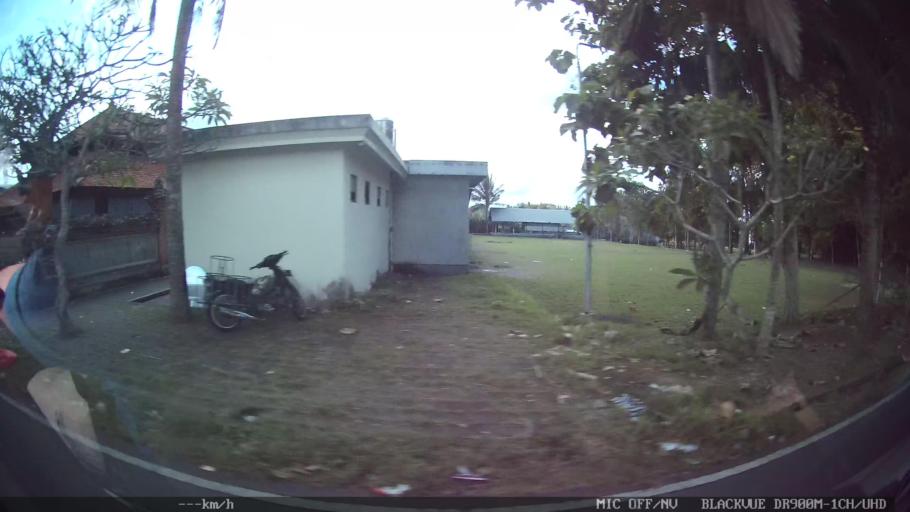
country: ID
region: Bali
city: Banjar Tebongkang
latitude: -8.5312
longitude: 115.2512
